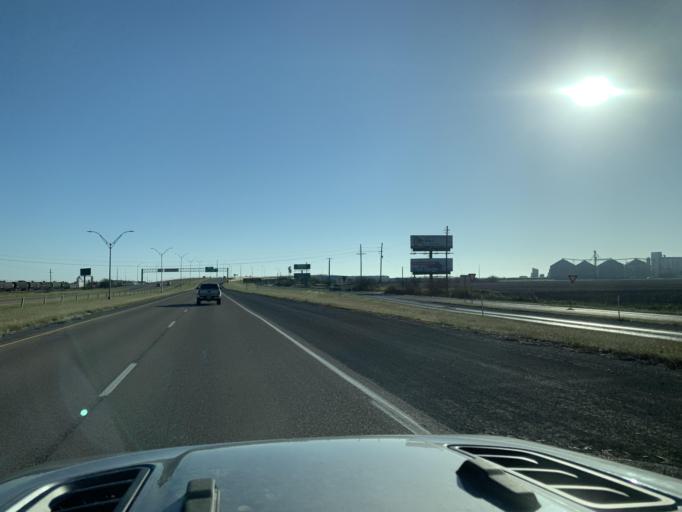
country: US
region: Texas
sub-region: Nueces County
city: Corpus Christi
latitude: 27.7848
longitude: -97.4929
